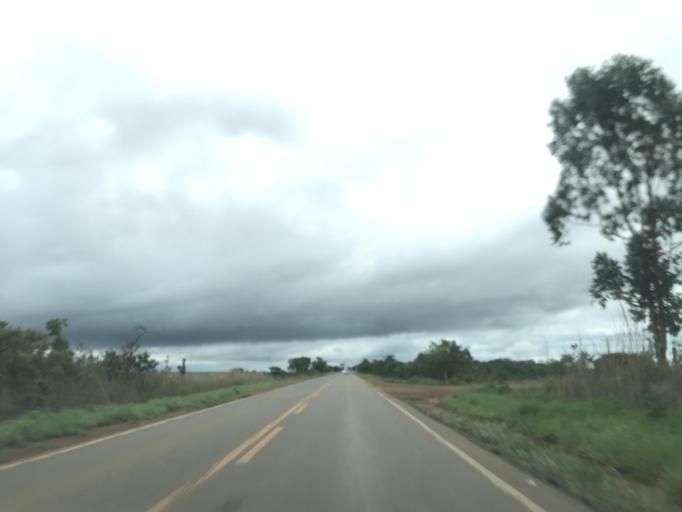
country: BR
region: Goias
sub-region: Luziania
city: Luziania
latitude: -16.4790
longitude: -48.2066
